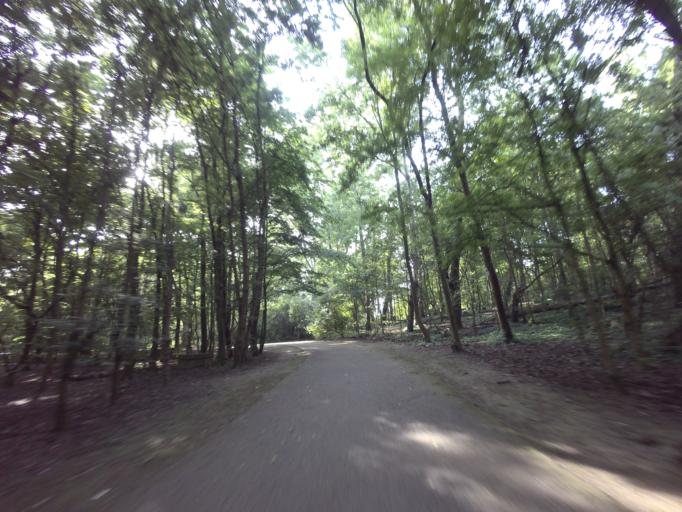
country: BE
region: Flanders
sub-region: Provincie Vlaams-Brabant
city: Diegem
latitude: 50.8804
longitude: 4.3964
